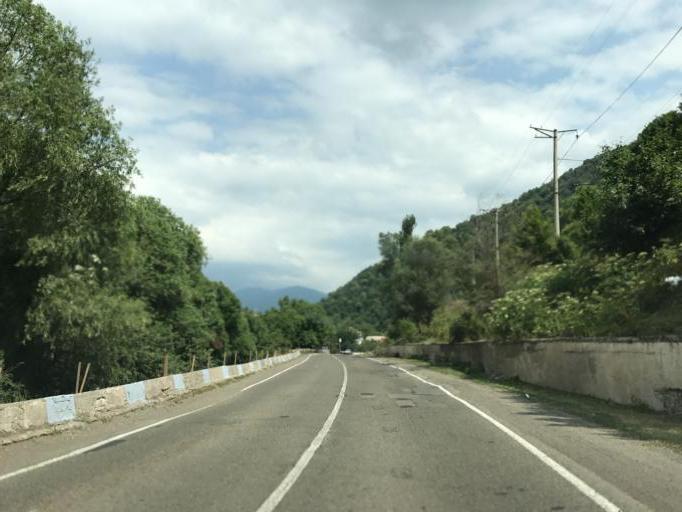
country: AM
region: Tavush
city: Haghartsin
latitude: 40.7740
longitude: 44.9466
